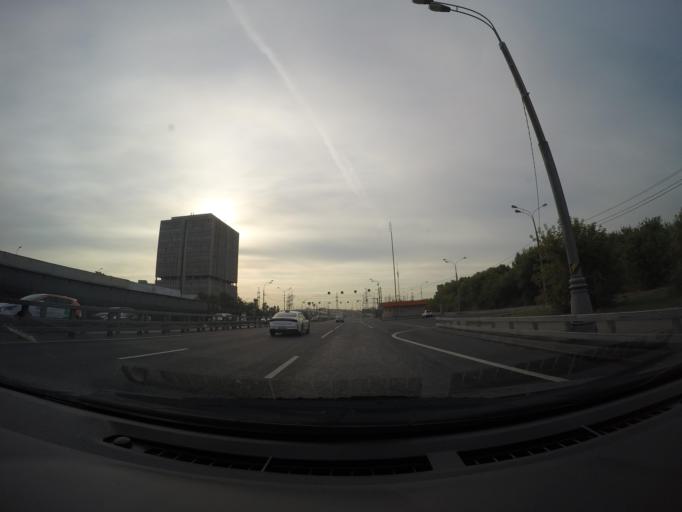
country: RU
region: Moscow
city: Veshnyaki
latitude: 55.7138
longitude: 37.8282
